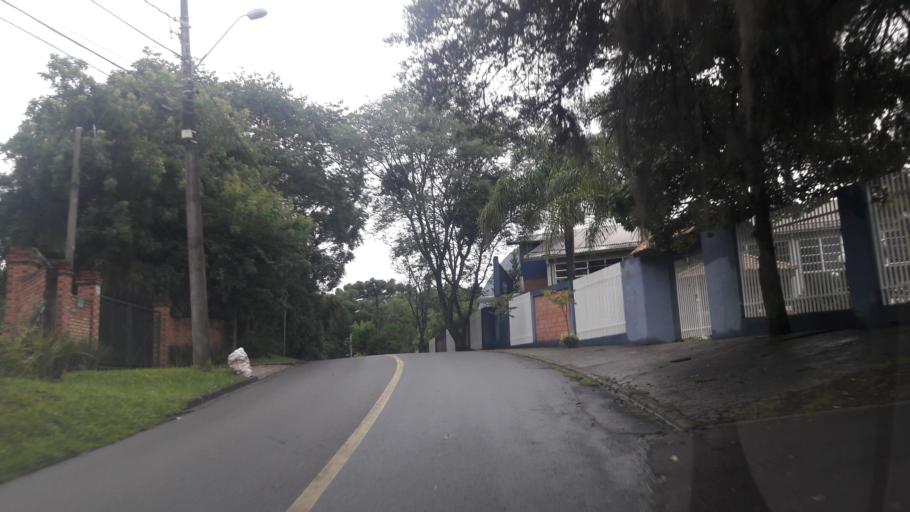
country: BR
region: Parana
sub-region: Curitiba
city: Curitiba
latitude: -25.3986
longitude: -49.3209
